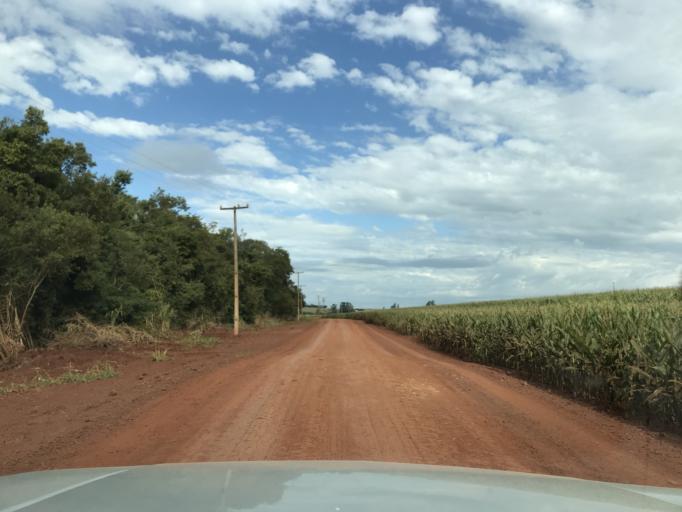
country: BR
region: Parana
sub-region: Palotina
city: Palotina
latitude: -24.3132
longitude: -53.8077
